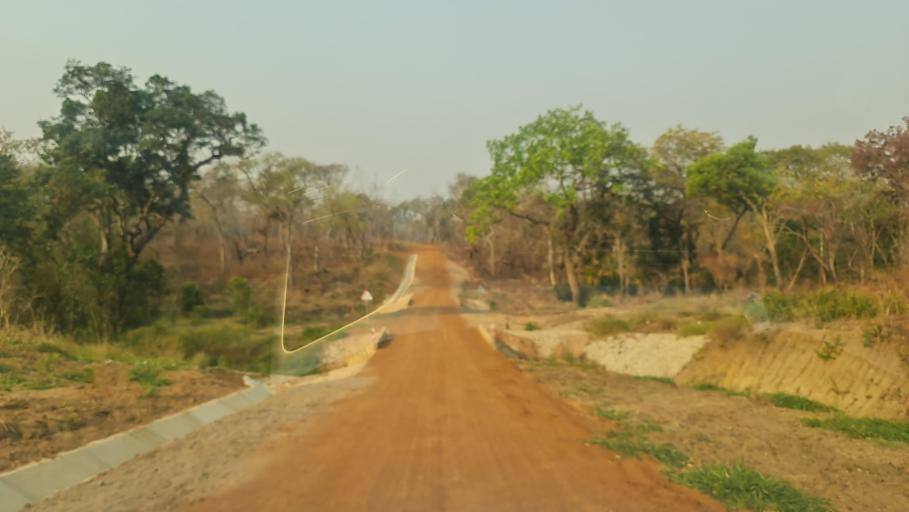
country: MZ
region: Zambezia
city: Quelimane
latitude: -17.1404
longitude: 37.1364
